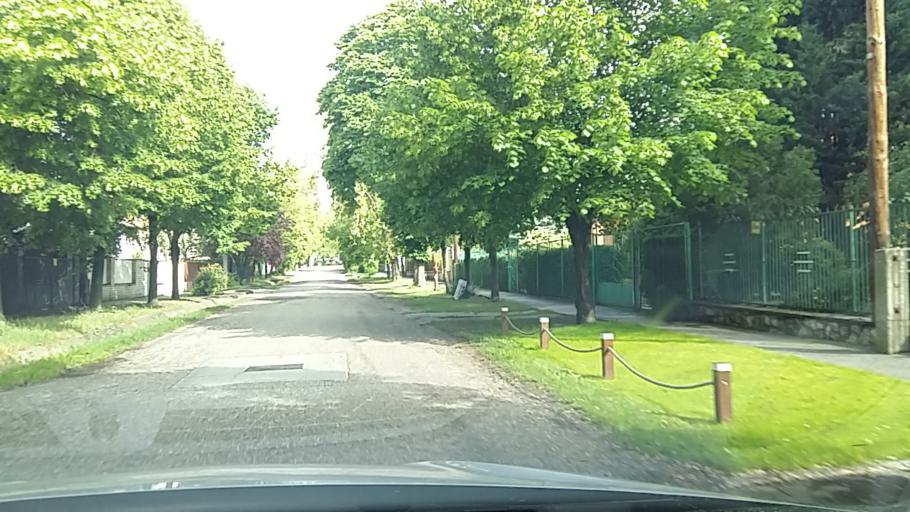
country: HU
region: Budapest
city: Budapest XVI. keruelet
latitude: 47.5057
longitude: 19.2057
